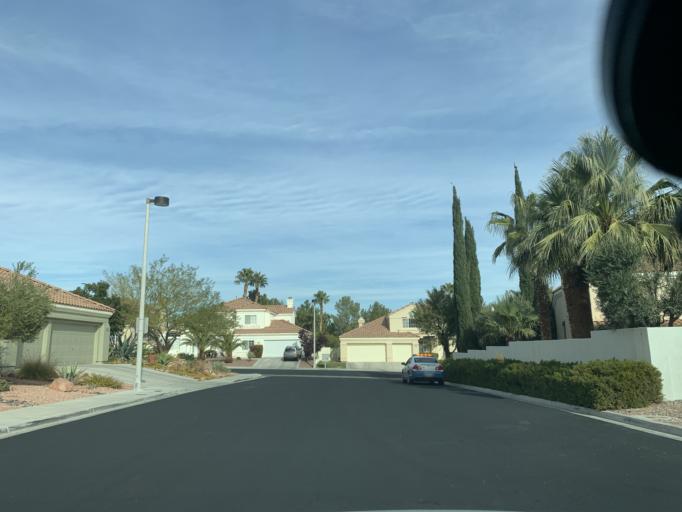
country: US
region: Nevada
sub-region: Clark County
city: Summerlin South
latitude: 36.1524
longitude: -115.2992
